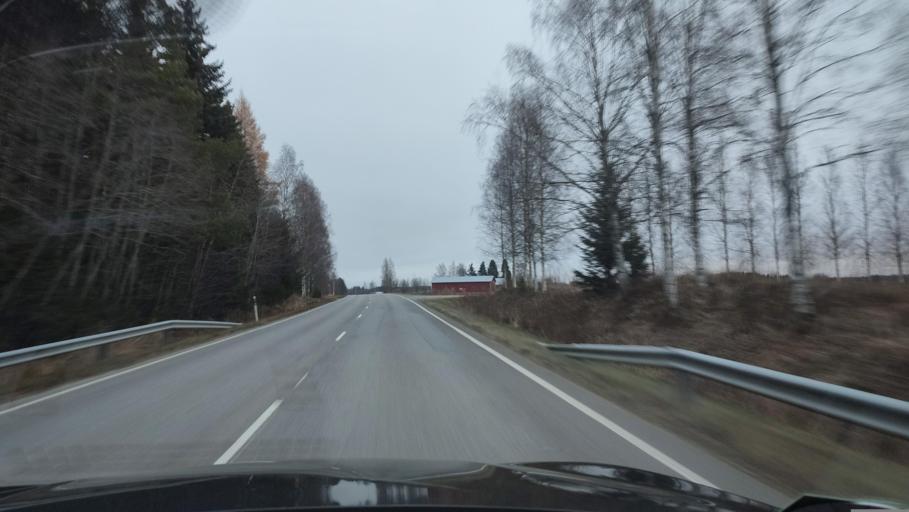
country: FI
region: Southern Ostrobothnia
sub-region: Suupohja
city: Kauhajoki
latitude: 62.3428
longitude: 22.0145
